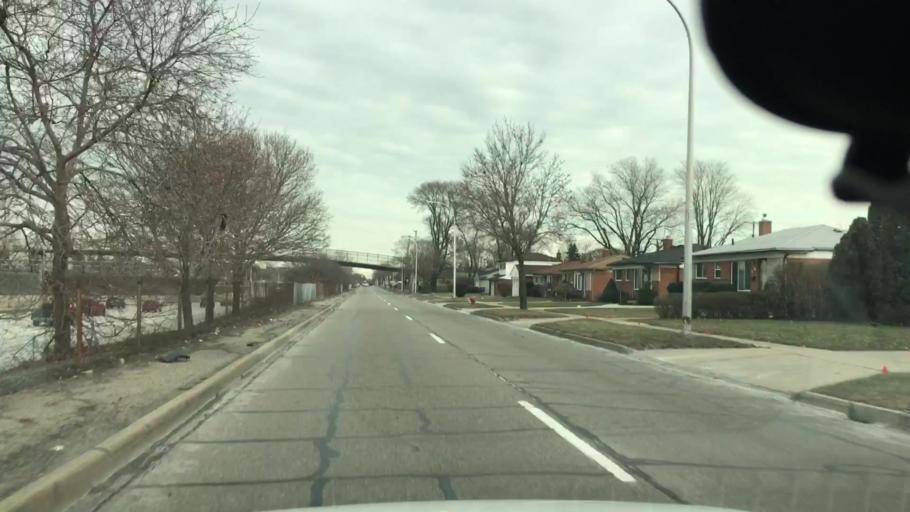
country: US
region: Michigan
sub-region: Oakland County
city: Madison Heights
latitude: 42.4907
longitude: -83.0737
